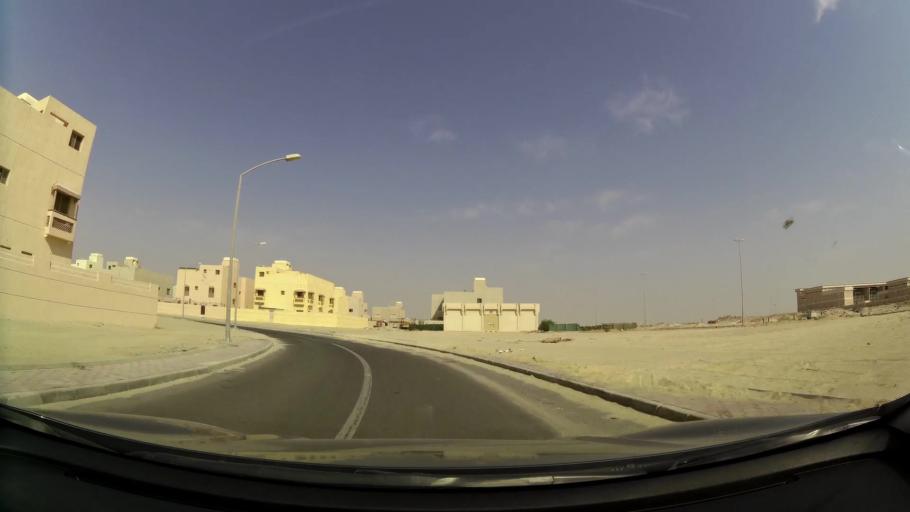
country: KW
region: Al Ahmadi
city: Al Wafrah
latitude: 28.8091
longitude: 48.0614
